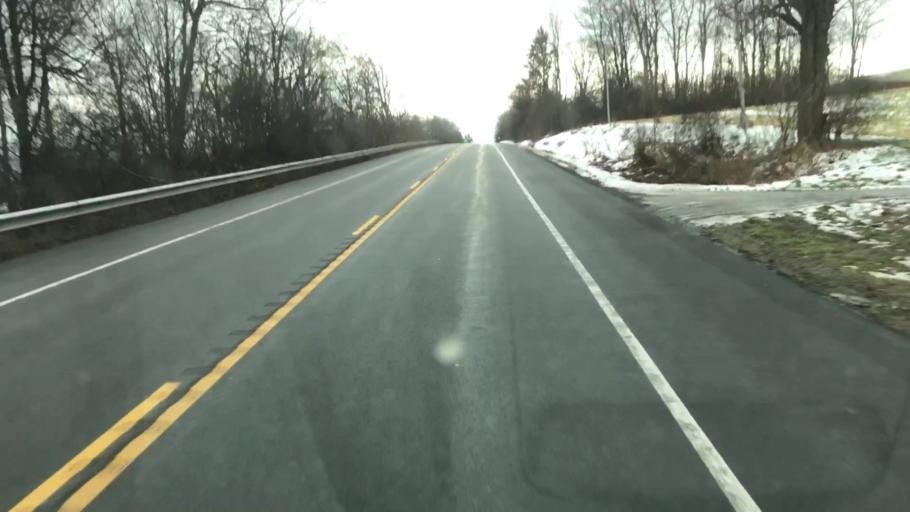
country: US
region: New York
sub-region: Onondaga County
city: Skaneateles
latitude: 42.9075
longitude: -76.4257
